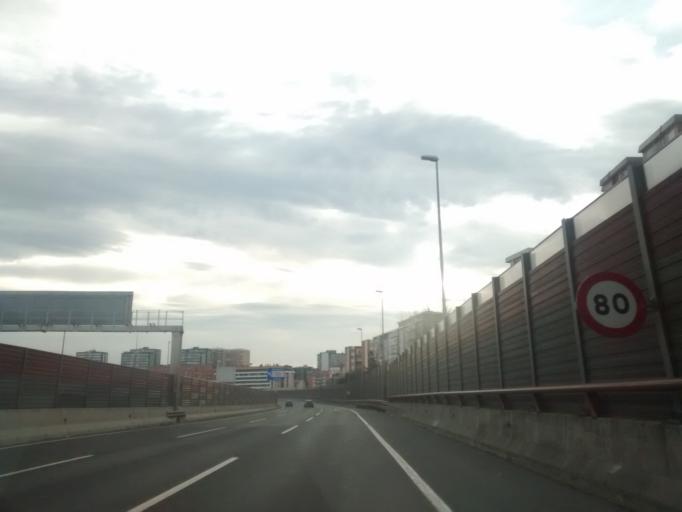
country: ES
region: Basque Country
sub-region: Bizkaia
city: Barakaldo
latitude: 43.2855
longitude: -2.9982
